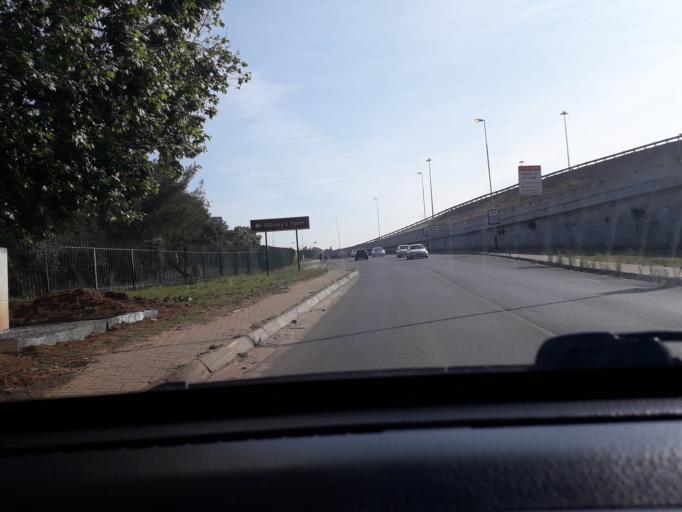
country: ZA
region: Gauteng
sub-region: Ekurhuleni Metropolitan Municipality
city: Germiston
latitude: -26.1692
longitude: 28.1310
